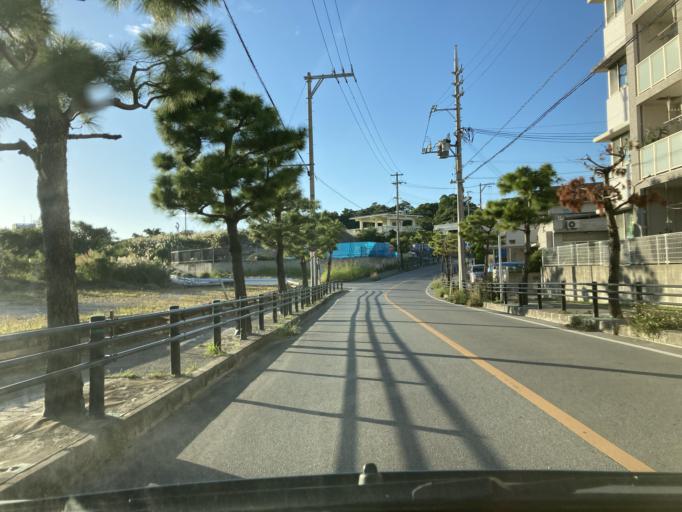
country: JP
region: Okinawa
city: Ginowan
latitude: 26.2530
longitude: 127.7707
